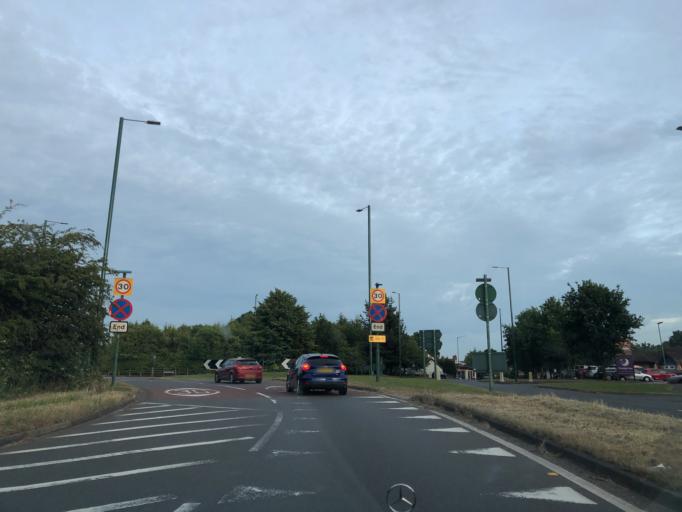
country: GB
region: England
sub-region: Solihull
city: Balsall Common
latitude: 52.4007
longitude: -1.6562
